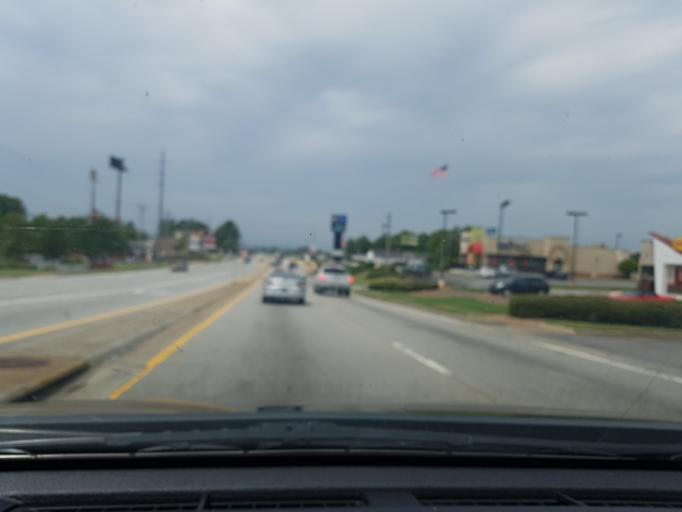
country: US
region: Georgia
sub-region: Gwinnett County
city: Suwanee
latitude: 34.0276
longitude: -84.0457
